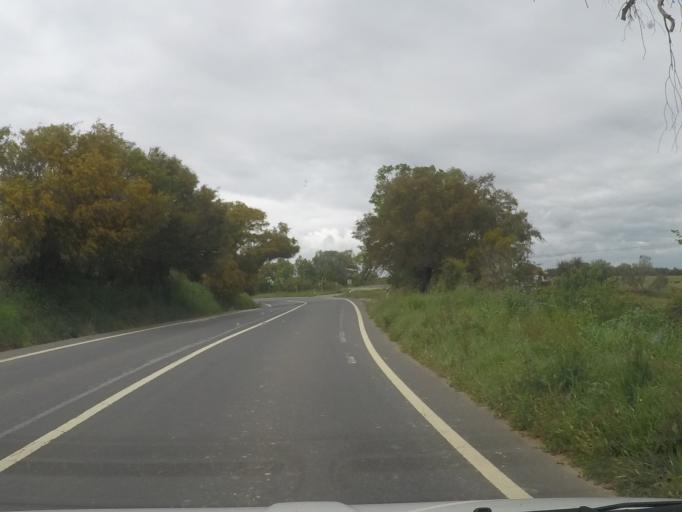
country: PT
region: Setubal
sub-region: Santiago do Cacem
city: Cercal
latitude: 37.8350
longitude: -8.7037
